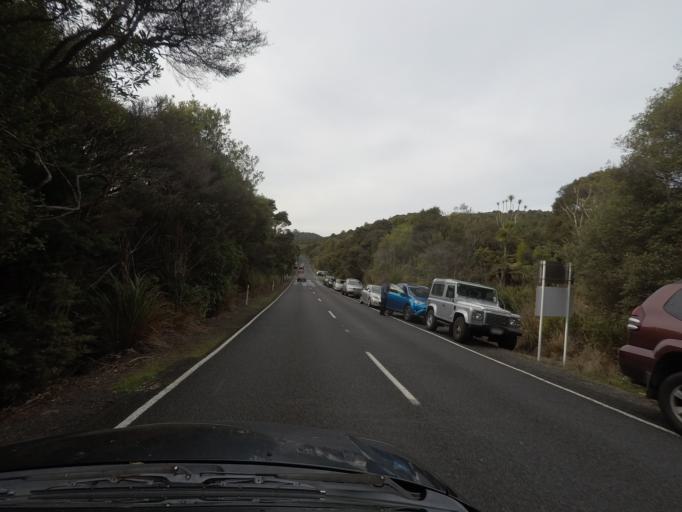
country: NZ
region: Auckland
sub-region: Auckland
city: Titirangi
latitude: -36.9365
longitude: 174.5575
